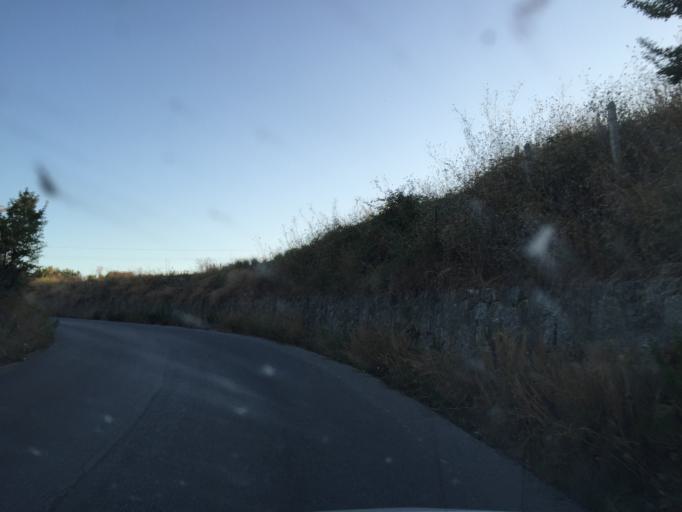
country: IT
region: Calabria
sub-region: Provincia di Vibo-Valentia
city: Pannaconi
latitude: 38.7153
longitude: 16.0492
